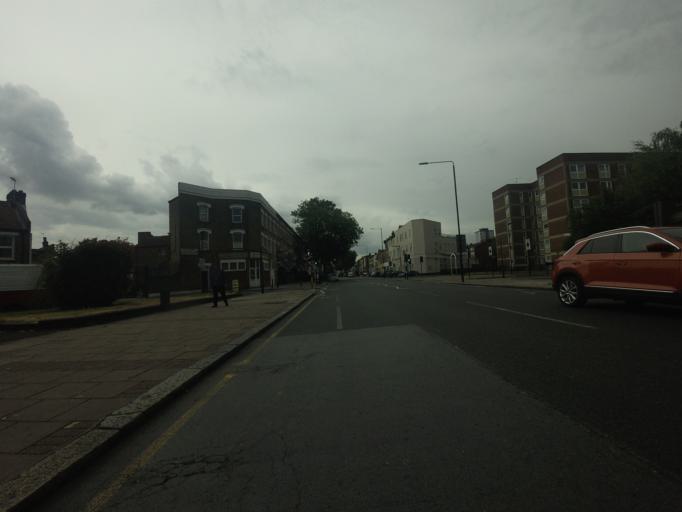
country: GB
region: England
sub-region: Greater London
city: Poplar
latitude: 51.5195
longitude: 0.0163
